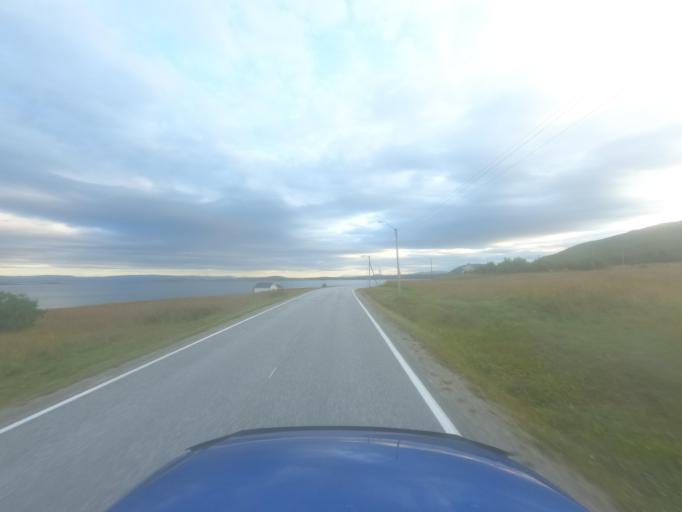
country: NO
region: Finnmark Fylke
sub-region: Porsanger
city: Lakselv
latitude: 70.4430
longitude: 25.2139
